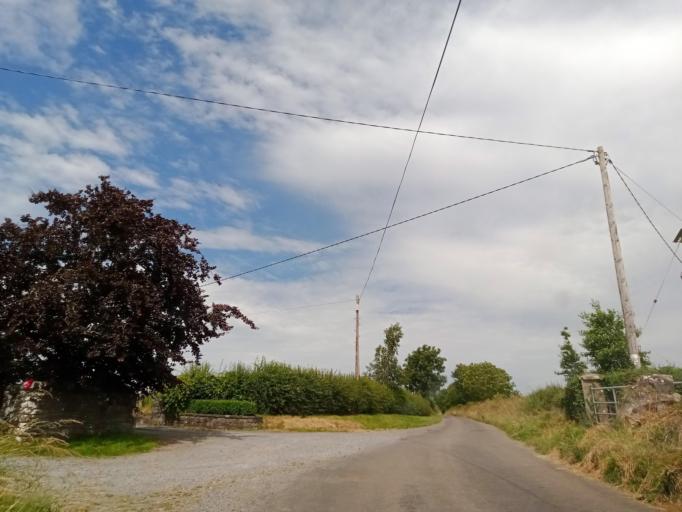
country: IE
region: Leinster
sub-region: Kilkenny
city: Thomastown
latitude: 52.5656
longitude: -7.1253
